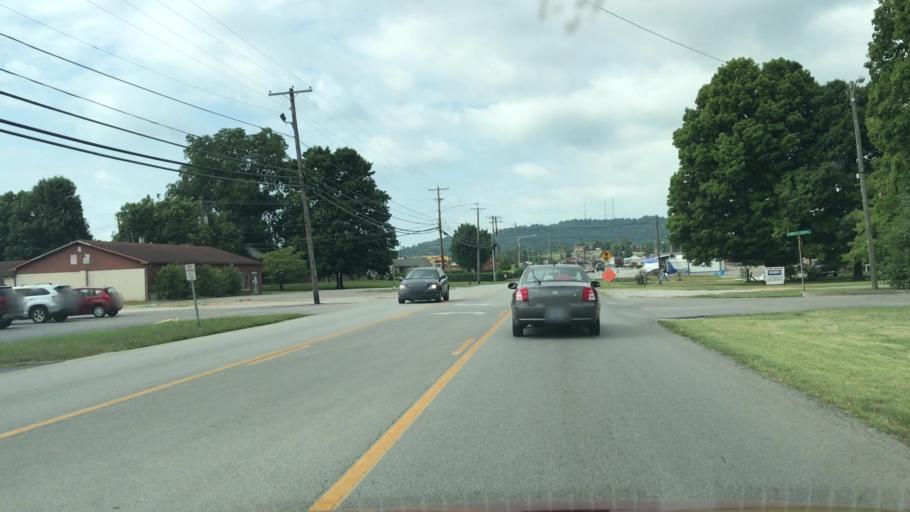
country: US
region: Kentucky
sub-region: Barren County
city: Cave City
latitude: 37.1306
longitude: -85.9607
